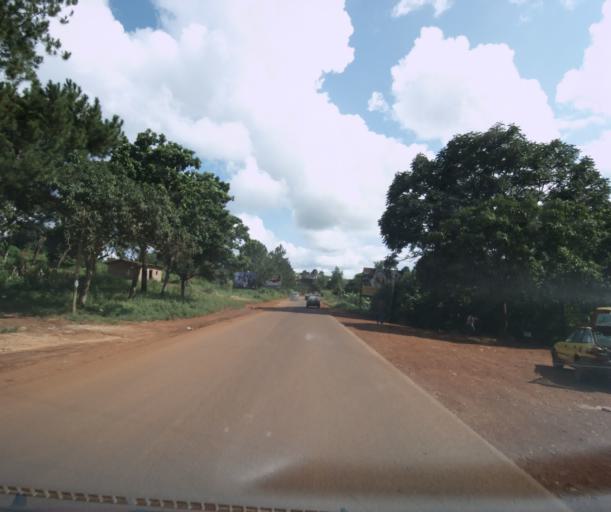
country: CM
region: West
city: Foumban
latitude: 5.7256
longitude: 10.8681
